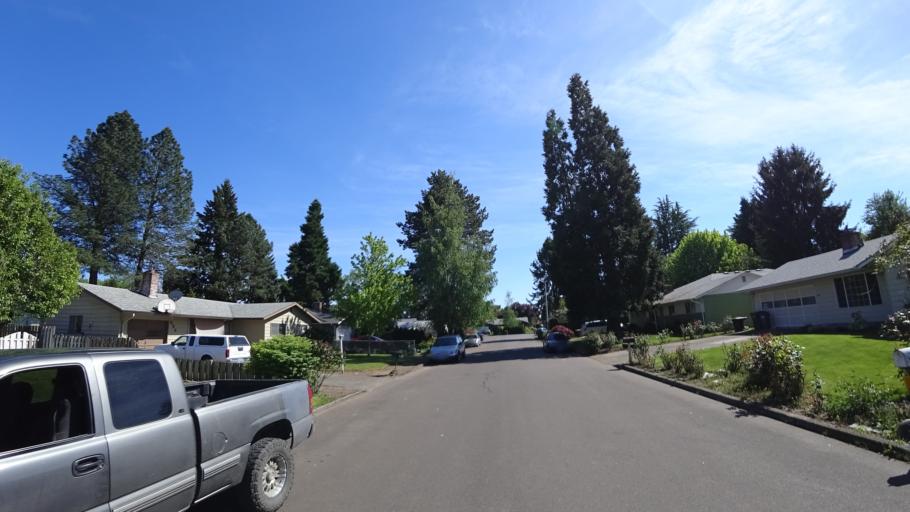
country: US
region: Oregon
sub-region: Washington County
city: Hillsboro
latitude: 45.5132
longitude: -122.9677
